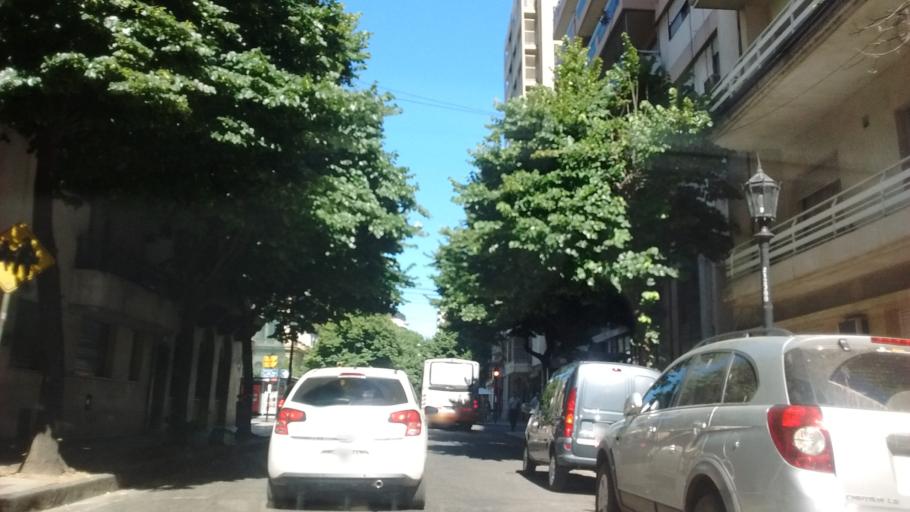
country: AR
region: Santa Fe
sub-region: Departamento de Rosario
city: Rosario
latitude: -32.9439
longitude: -60.6525
